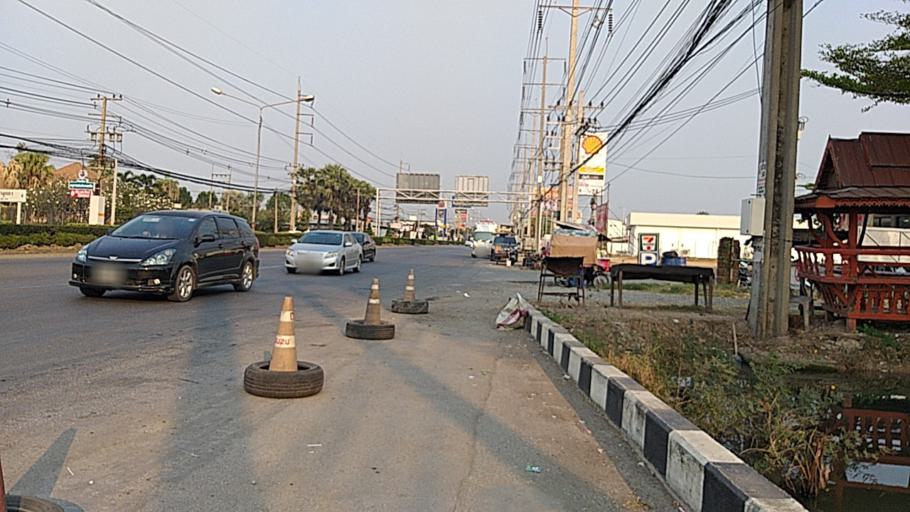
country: TH
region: Pathum Thani
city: Lam Luk Ka
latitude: 13.9338
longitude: 100.7151
